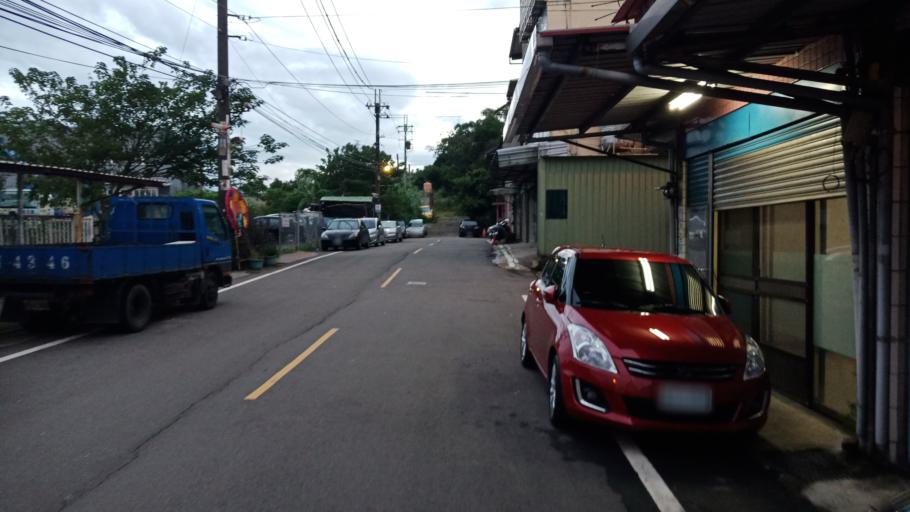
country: TW
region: Taiwan
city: Daxi
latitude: 24.8706
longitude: 121.1978
